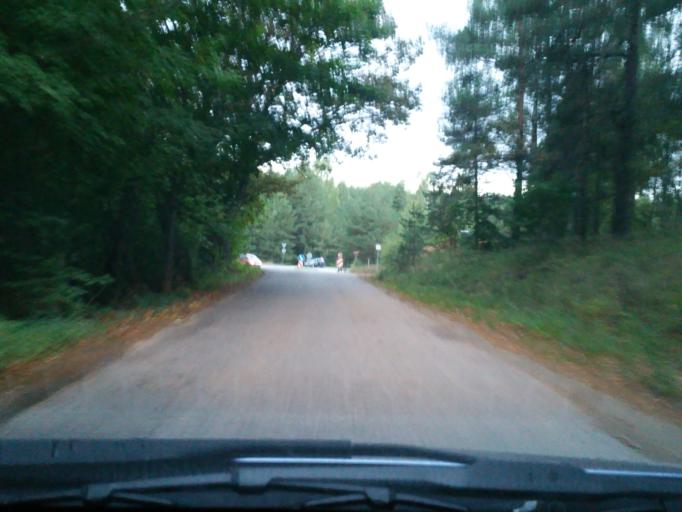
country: LV
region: Adazi
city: Adazi
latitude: 57.1258
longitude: 24.3304
